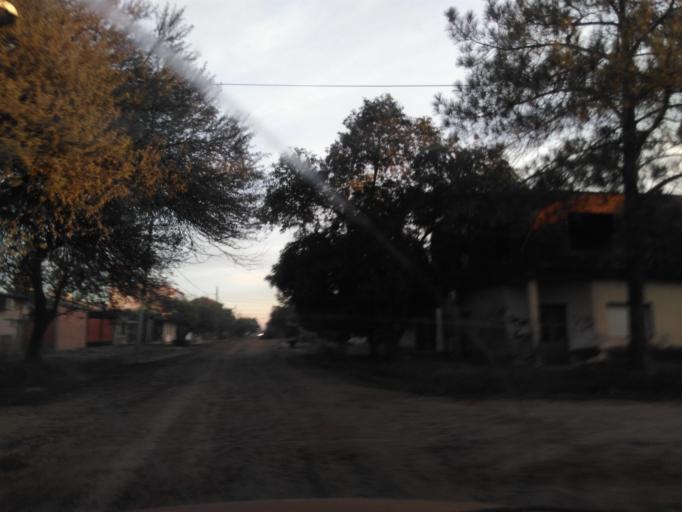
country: AR
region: Chaco
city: Resistencia
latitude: -27.4639
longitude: -59.0025
